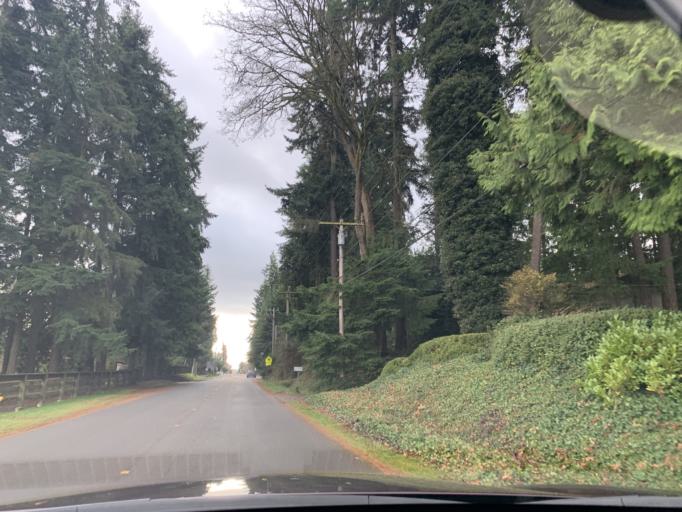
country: US
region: Washington
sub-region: King County
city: Kingsgate
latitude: 47.7316
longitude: -122.1639
